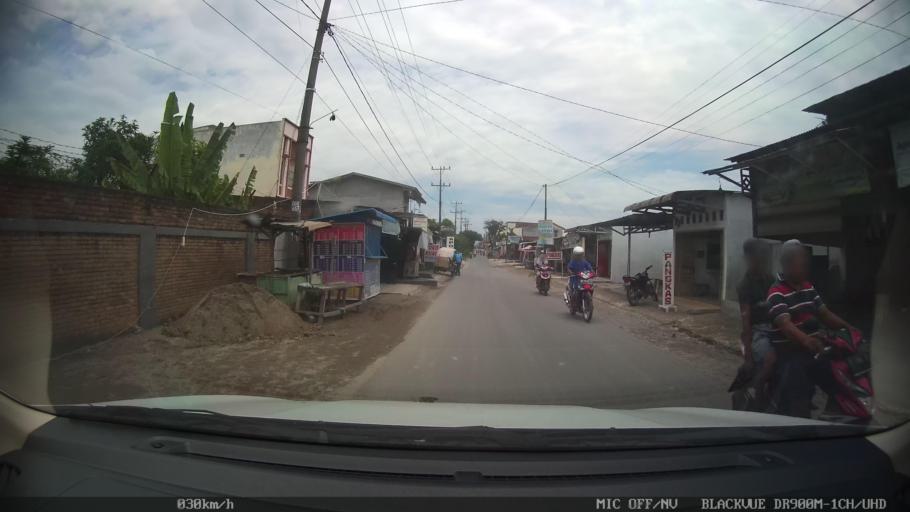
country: ID
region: North Sumatra
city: Sunggal
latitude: 3.6079
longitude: 98.5801
